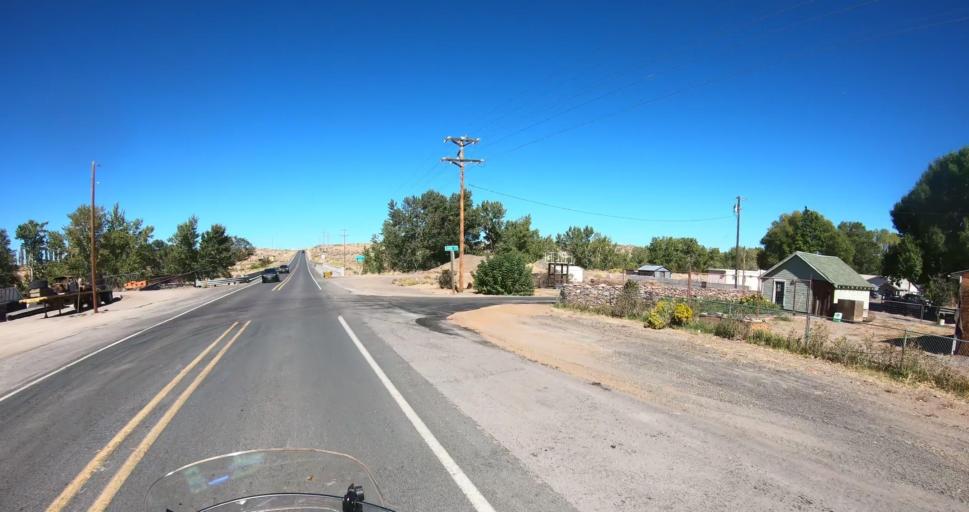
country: US
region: Oregon
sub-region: Lake County
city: Lakeview
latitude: 42.6947
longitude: -120.5457
